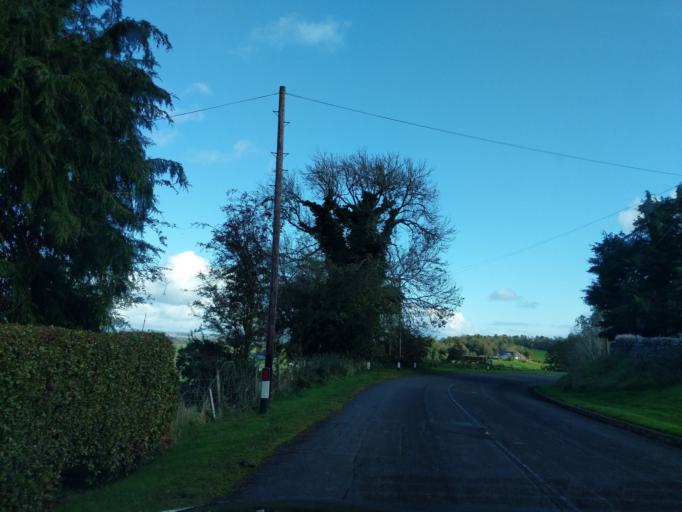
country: GB
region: Scotland
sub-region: Dumfries and Galloway
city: Dumfries
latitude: 55.0612
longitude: -3.6838
